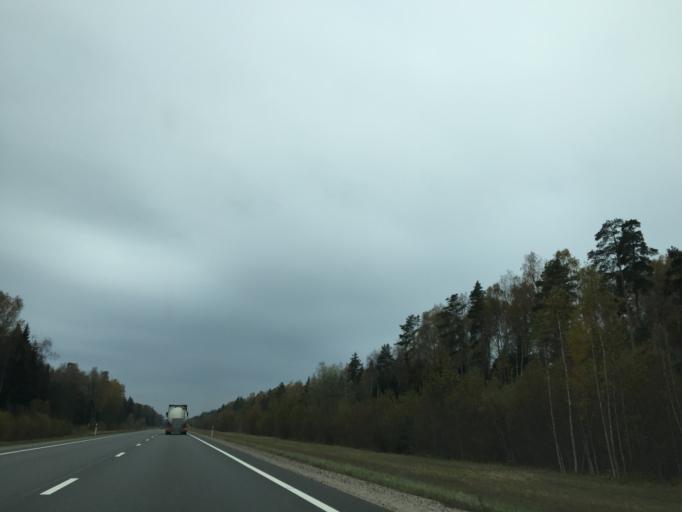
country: LV
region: Ozolnieku
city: Ozolnieki
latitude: 56.7127
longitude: 23.8422
